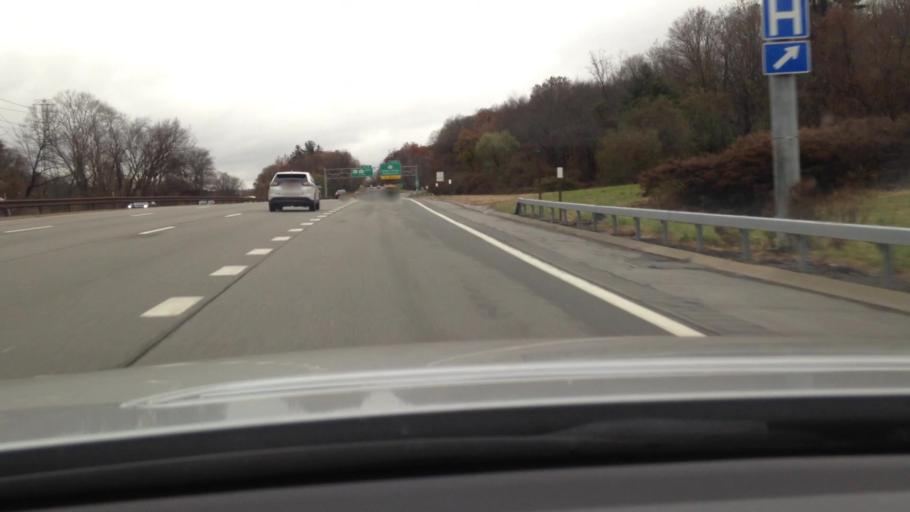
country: US
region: New York
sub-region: Westchester County
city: Hawthorne
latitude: 41.1161
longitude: -73.8058
